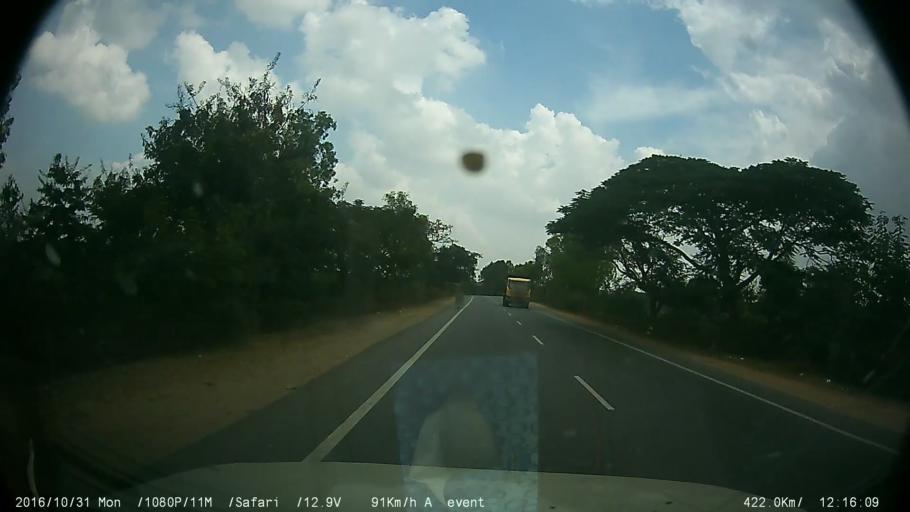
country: IN
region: Karnataka
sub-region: Mysore
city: Hunsur
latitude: 12.3361
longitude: 76.3853
